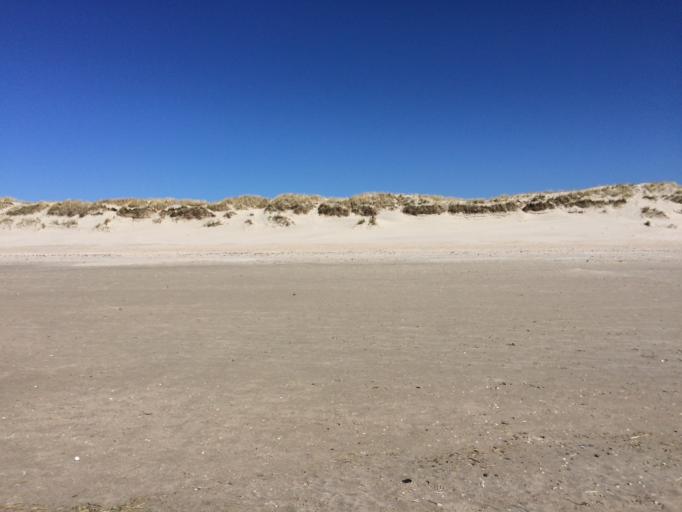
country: DK
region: South Denmark
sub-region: Varde Kommune
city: Oksbol
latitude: 55.5523
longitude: 8.0962
